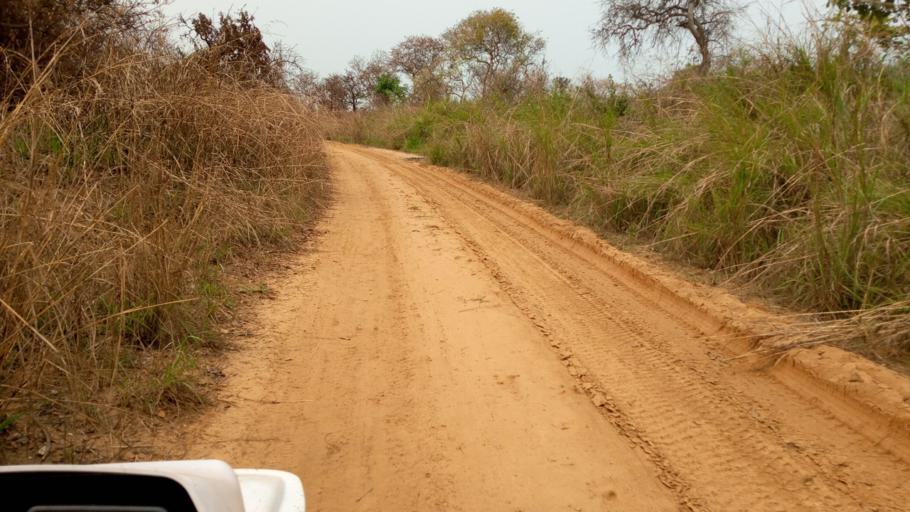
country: CD
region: Bandundu
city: Bandundu
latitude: -3.4570
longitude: 17.7689
